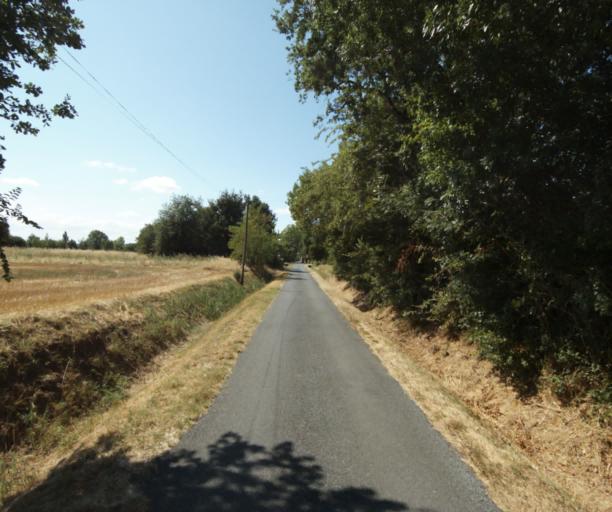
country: FR
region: Midi-Pyrenees
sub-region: Departement de la Haute-Garonne
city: Revel
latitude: 43.4997
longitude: 2.0003
